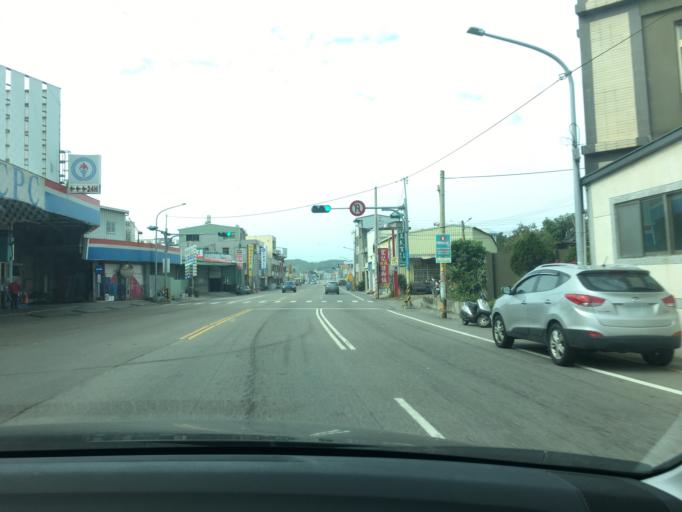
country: TW
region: Taiwan
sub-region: Miaoli
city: Miaoli
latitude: 24.4963
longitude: 120.7014
